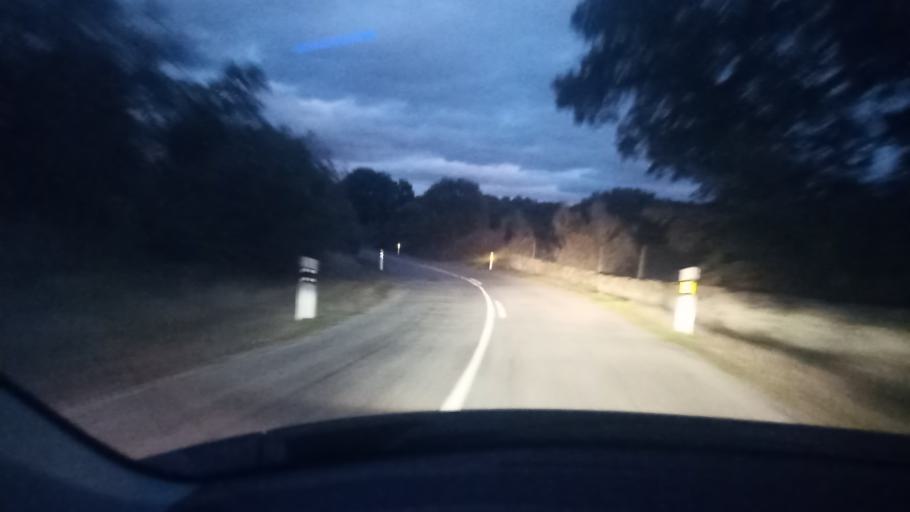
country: ES
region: Madrid
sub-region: Provincia de Madrid
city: Colmenar del Arroyo
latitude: 40.4296
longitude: -4.2195
